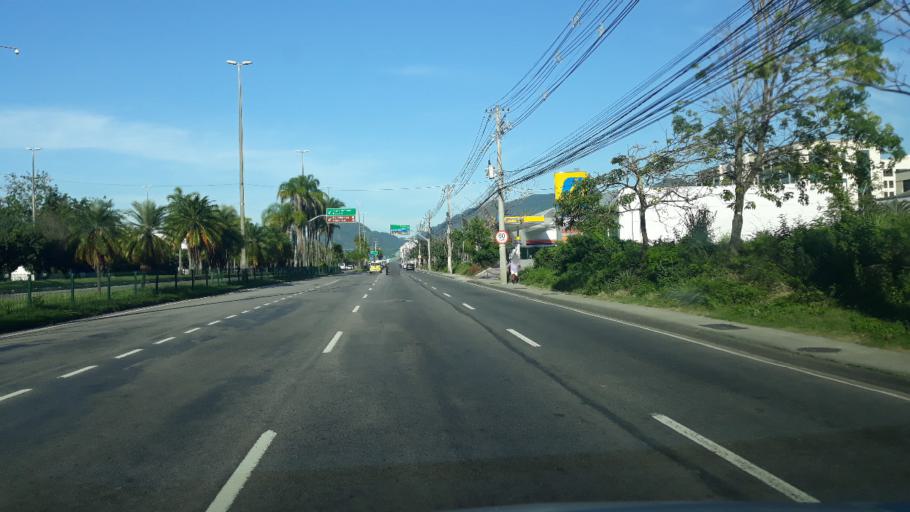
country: BR
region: Rio de Janeiro
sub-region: Sao Joao De Meriti
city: Sao Joao de Meriti
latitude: -22.9732
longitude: -43.3680
